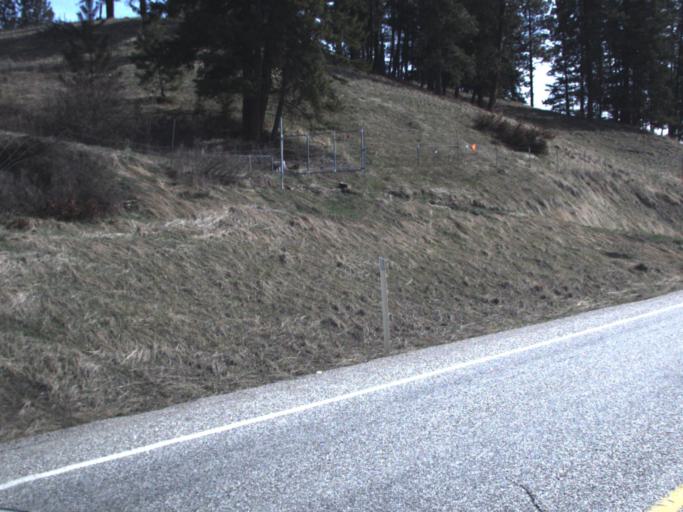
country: US
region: Washington
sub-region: Stevens County
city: Colville
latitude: 48.5158
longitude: -117.7898
